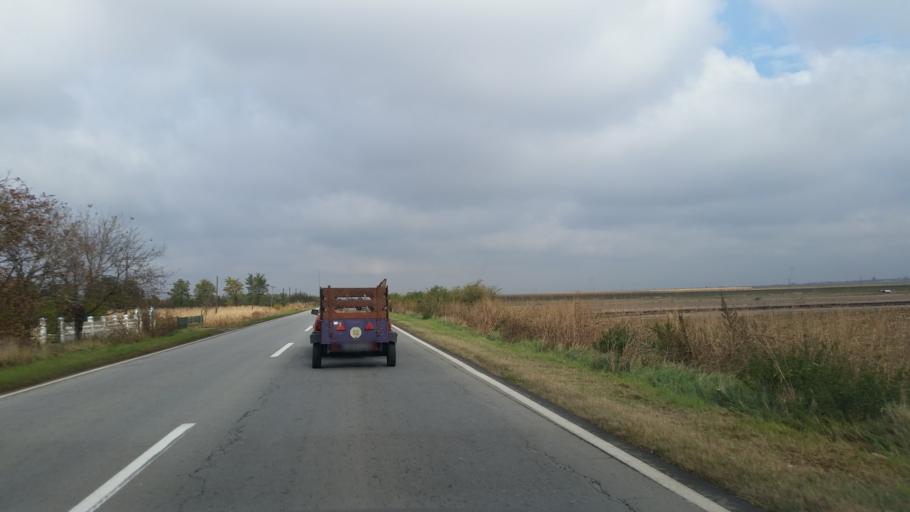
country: RS
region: Autonomna Pokrajina Vojvodina
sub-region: Srednjebanatski Okrug
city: Zrenjanin
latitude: 45.4221
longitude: 20.3711
